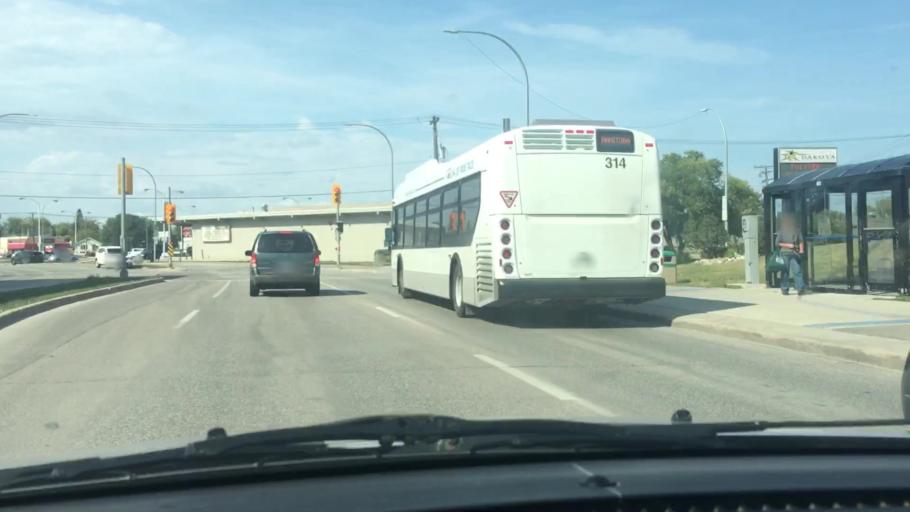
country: CA
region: Manitoba
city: Winnipeg
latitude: 49.8348
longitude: -97.1105
